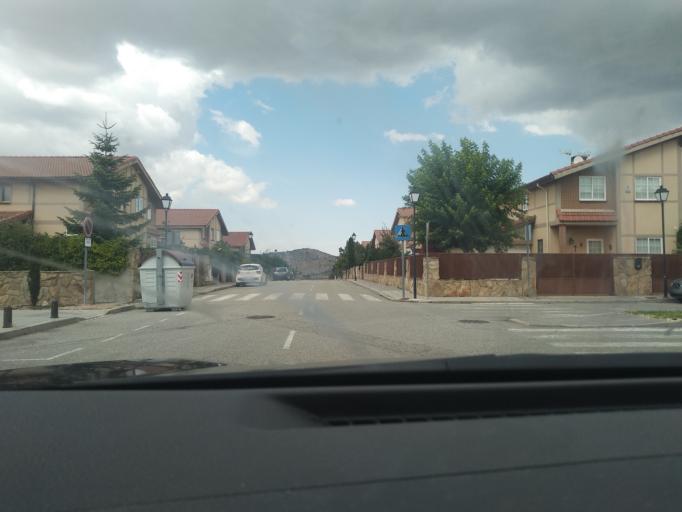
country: ES
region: Castille and Leon
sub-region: Provincia de Segovia
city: Otero de Herreros
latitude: 40.7411
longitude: -4.1878
